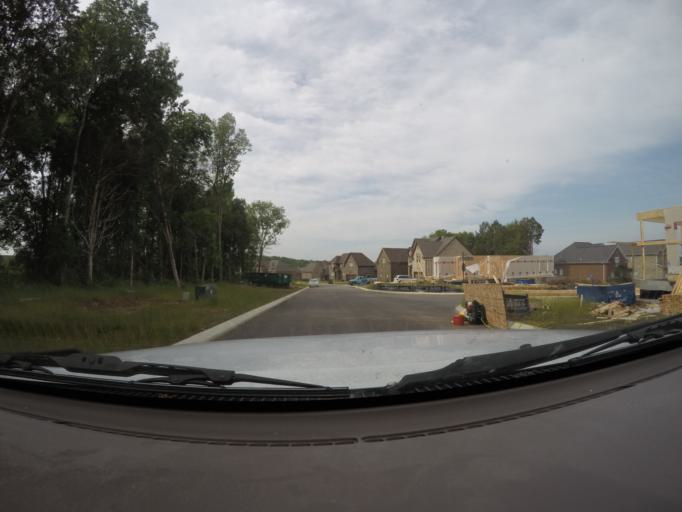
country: US
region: Tennessee
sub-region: Wilson County
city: Mount Juliet
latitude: 36.2206
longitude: -86.4866
